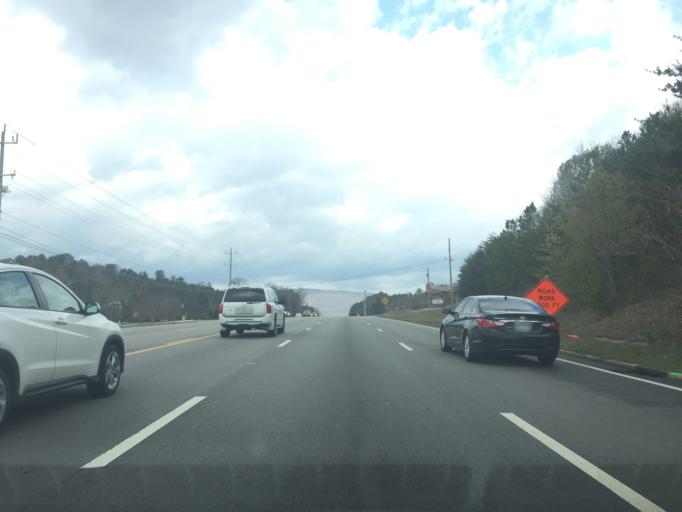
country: US
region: Tennessee
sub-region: Hamilton County
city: Falling Water
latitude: 35.1659
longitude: -85.2480
